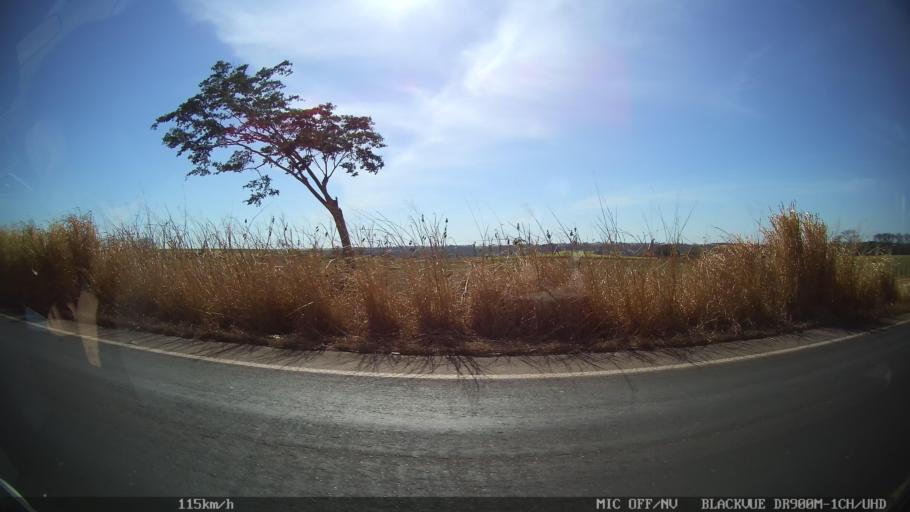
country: BR
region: Sao Paulo
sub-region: Olimpia
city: Olimpia
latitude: -20.6220
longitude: -48.7703
